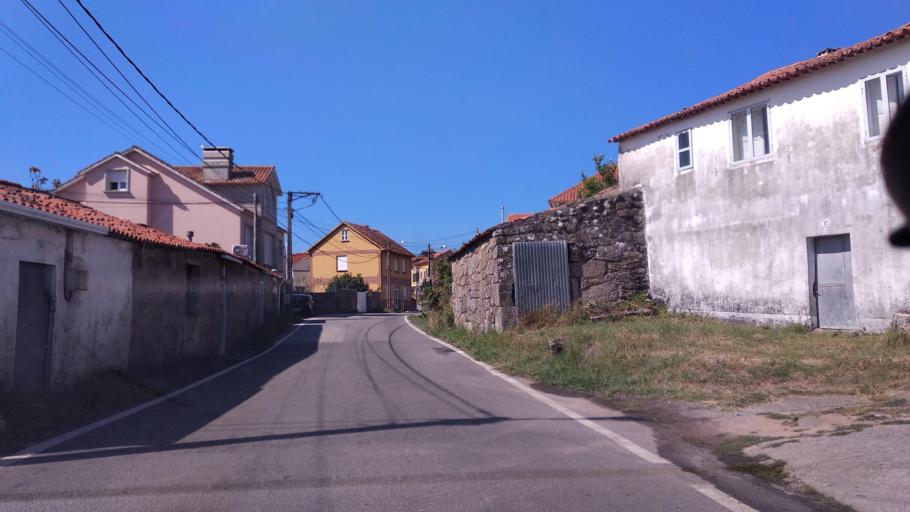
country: ES
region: Galicia
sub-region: Provincia de Pontevedra
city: Moana
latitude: 42.2780
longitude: -8.7690
